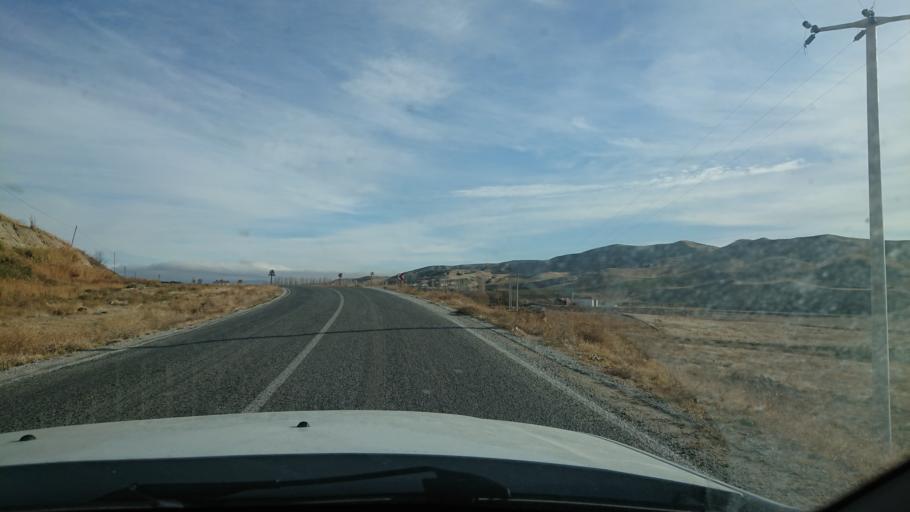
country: TR
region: Aksaray
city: Acipinar
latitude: 38.4861
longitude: 33.9167
